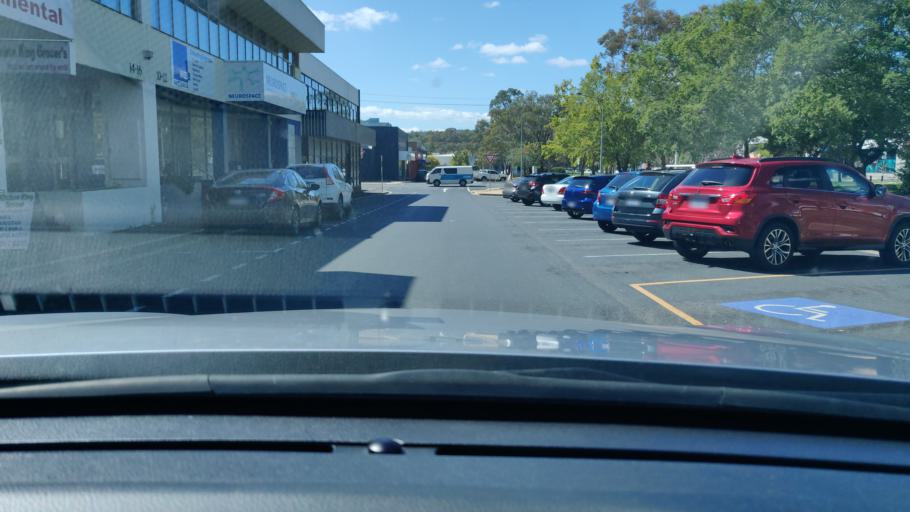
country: AU
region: Australian Capital Territory
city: Forrest
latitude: -35.3523
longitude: 149.0872
